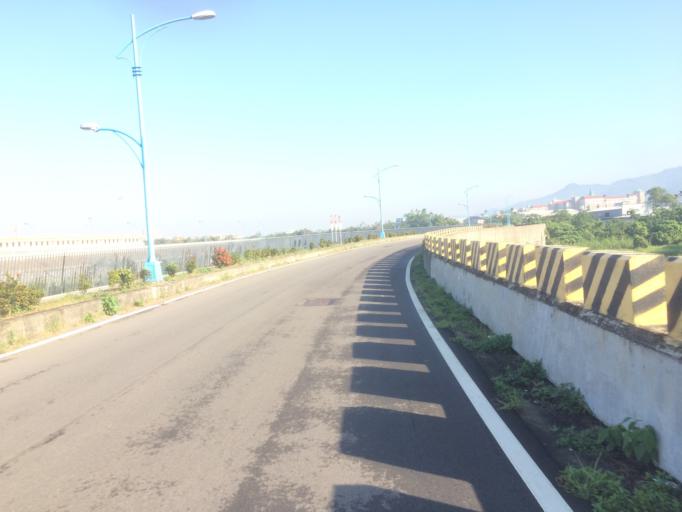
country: TW
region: Taiwan
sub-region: Taichung City
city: Taichung
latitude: 24.1875
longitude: 120.7113
